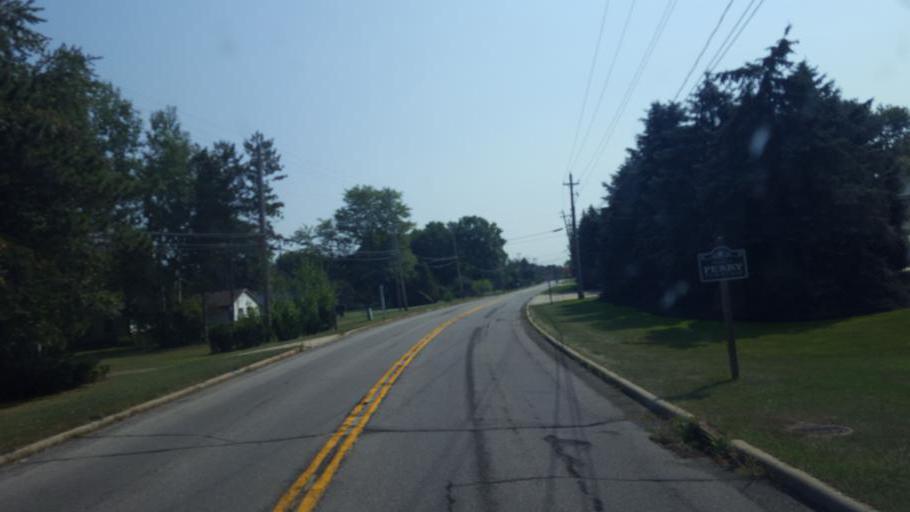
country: US
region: Ohio
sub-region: Lake County
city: Painesville
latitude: 41.7269
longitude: -81.1912
